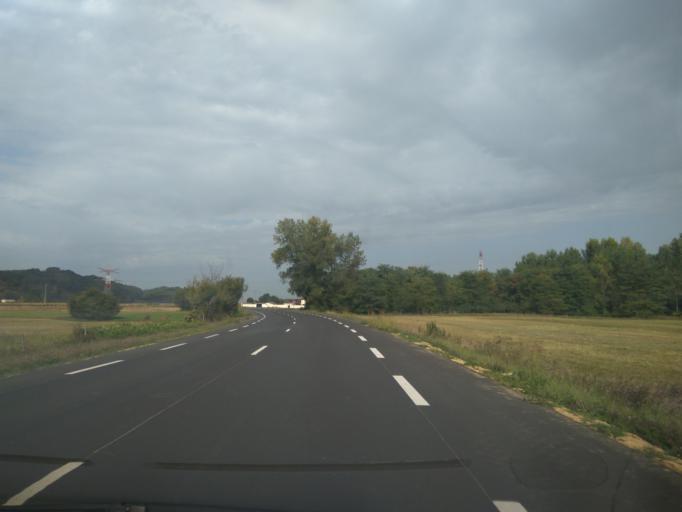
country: FR
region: Aquitaine
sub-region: Departement des Pyrenees-Atlantiques
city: Arbus
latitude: 43.3362
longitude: -0.4969
